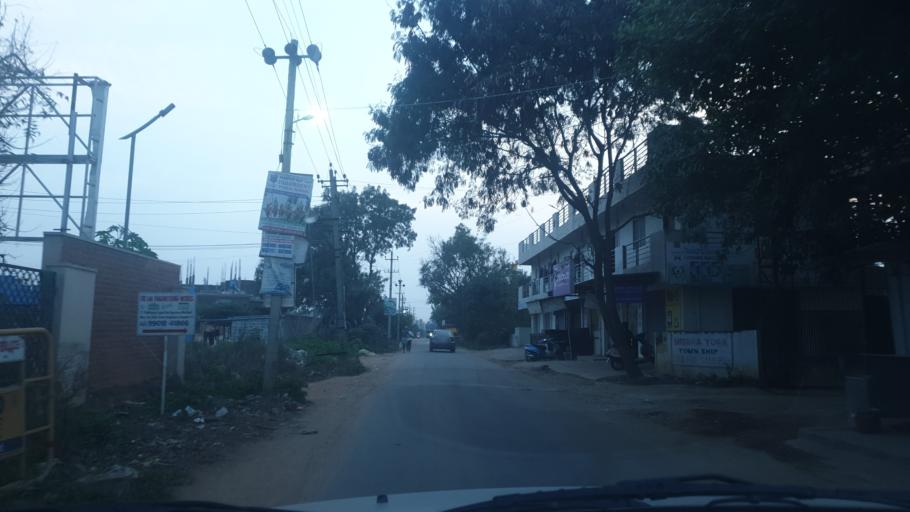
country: IN
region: Karnataka
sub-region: Bangalore Urban
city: Yelahanka
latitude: 13.0679
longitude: 77.6896
